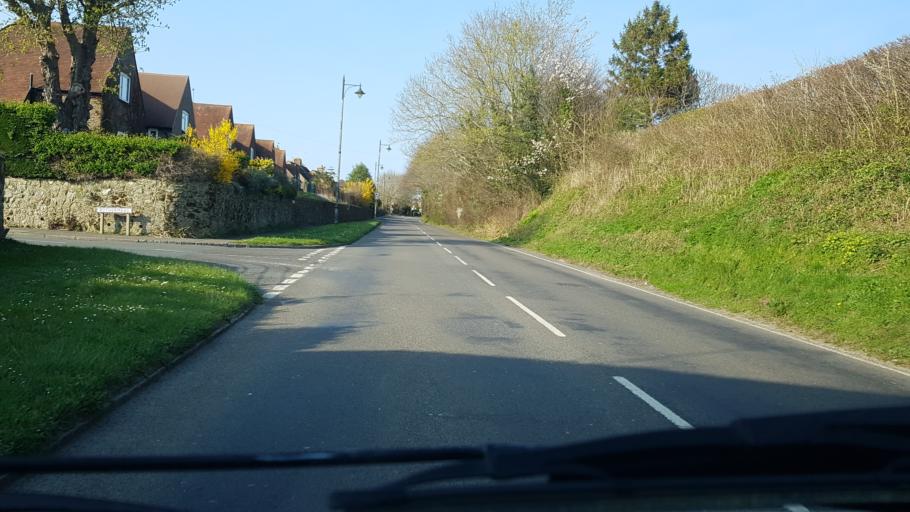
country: GB
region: England
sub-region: West Sussex
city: Petworth
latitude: 50.9797
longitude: -0.6124
